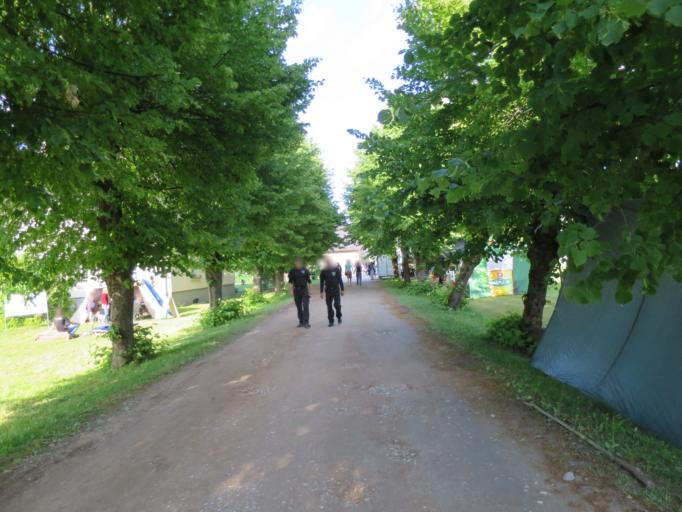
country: LV
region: Ligatne
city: Ligatne
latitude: 57.2230
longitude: 24.9613
